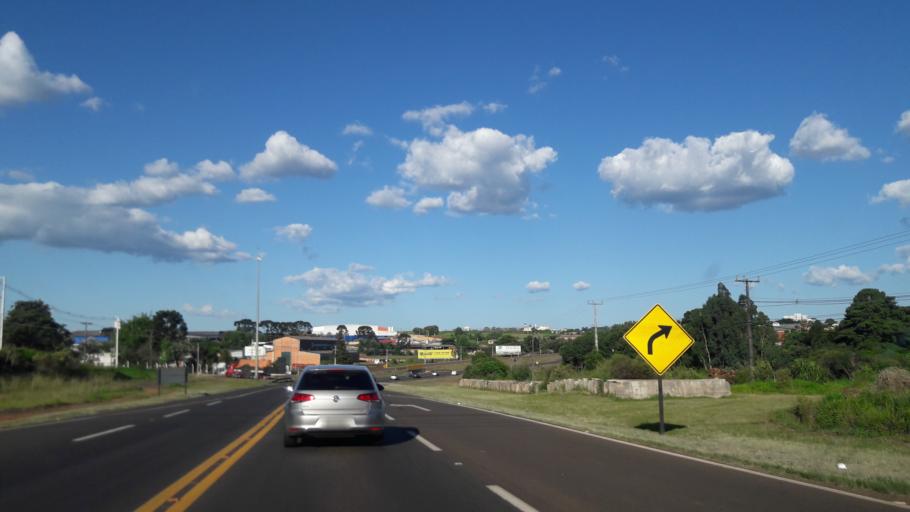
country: BR
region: Parana
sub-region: Guarapuava
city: Guarapuava
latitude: -25.3672
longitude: -51.4933
